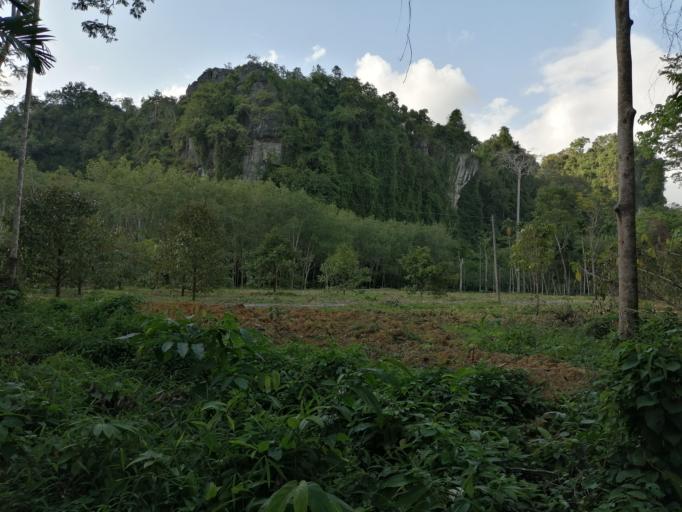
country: TH
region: Nakhon Si Thammarat
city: Thung Song
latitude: 8.1005
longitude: 99.7433
